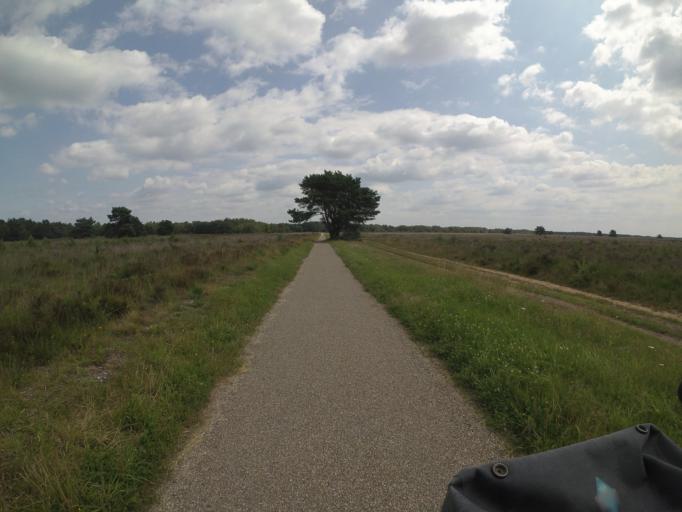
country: NL
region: Gelderland
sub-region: Gemeente Barneveld
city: Garderen
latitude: 52.2669
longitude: 5.7298
